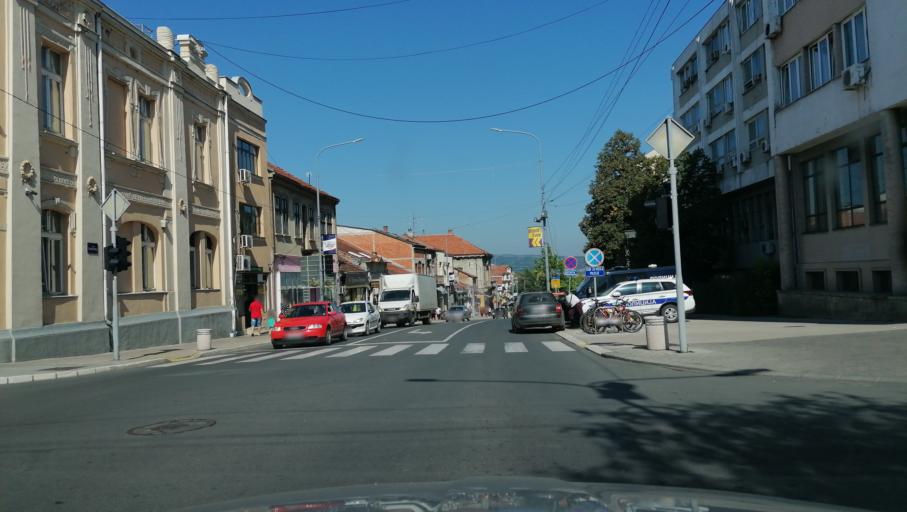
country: RS
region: Central Serbia
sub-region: Rasinski Okrug
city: Krusevac
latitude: 43.5839
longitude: 21.3245
